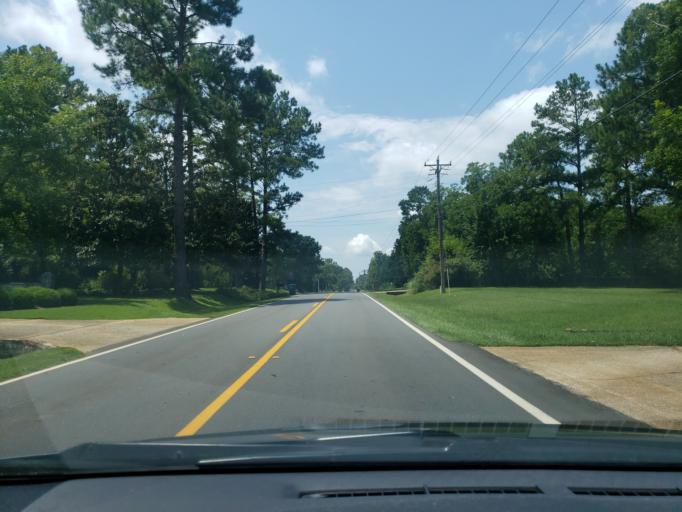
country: US
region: Georgia
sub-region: Dougherty County
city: Albany
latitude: 31.6130
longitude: -84.2699
